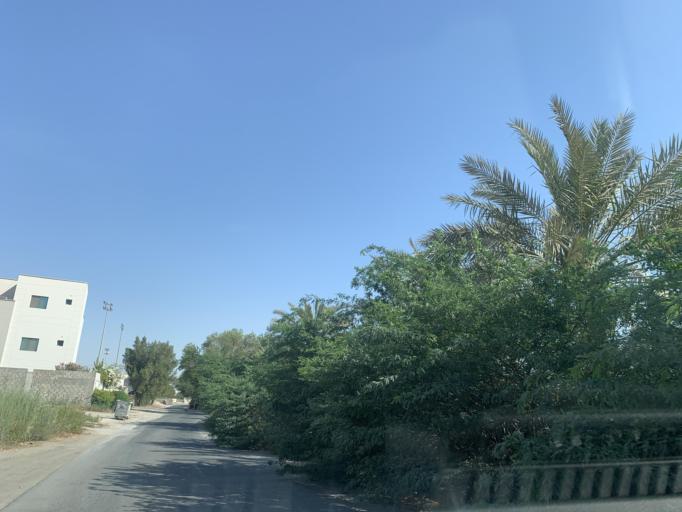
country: BH
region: Northern
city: Madinat `Isa
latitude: 26.1937
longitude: 50.4692
